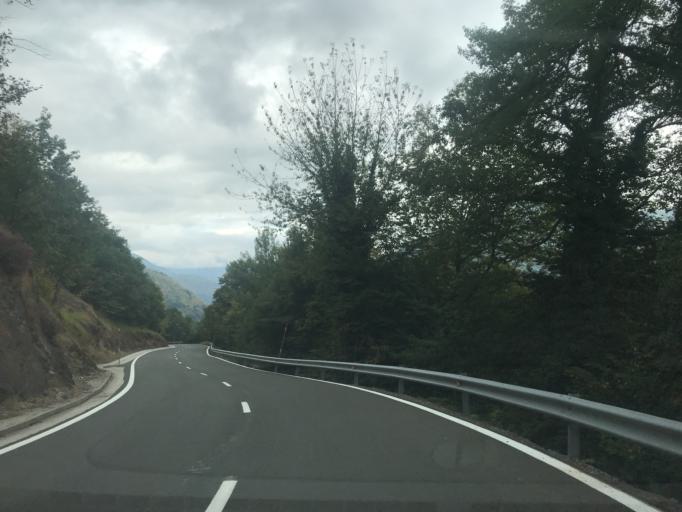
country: ES
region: Catalonia
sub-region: Provincia de Lleida
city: Les
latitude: 42.7709
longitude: 0.6766
